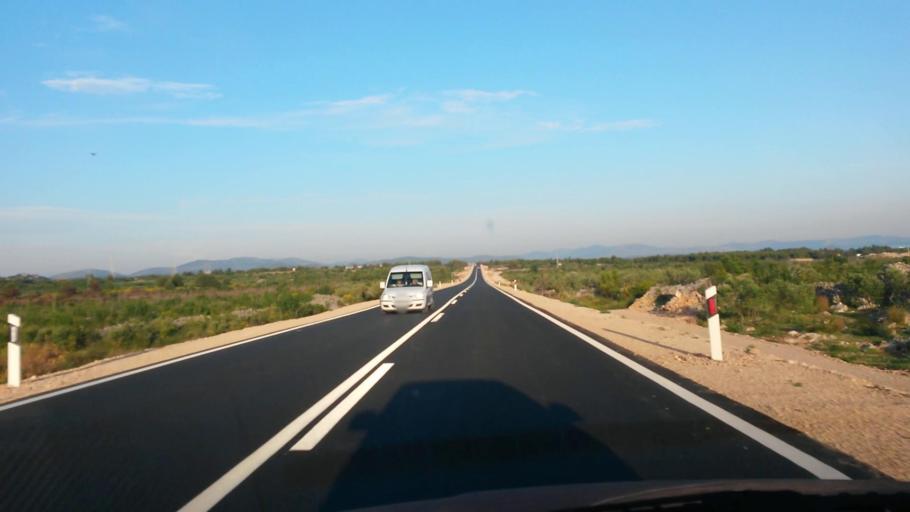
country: HR
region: Sibensko-Kniniska
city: Vodice
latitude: 43.7715
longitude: 15.7894
